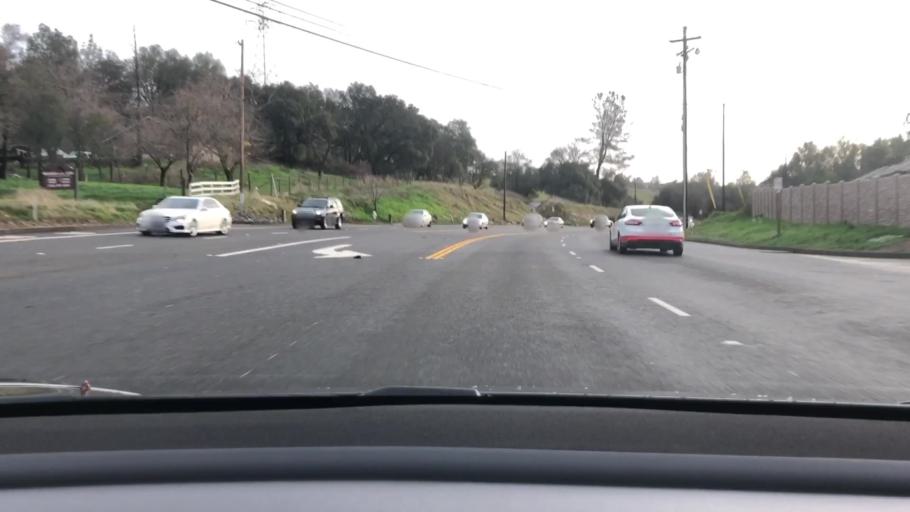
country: US
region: California
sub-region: Placer County
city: Granite Bay
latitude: 38.7335
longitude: -121.1706
